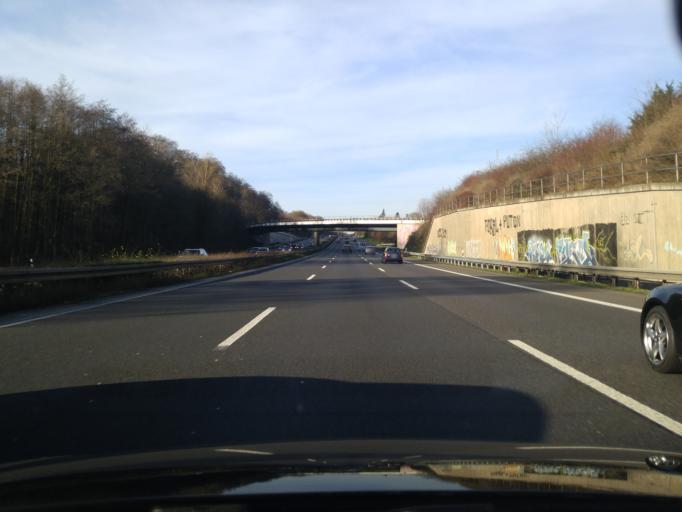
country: DE
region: North Rhine-Westphalia
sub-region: Regierungsbezirk Koln
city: Rosrath
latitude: 50.8826
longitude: 7.1857
